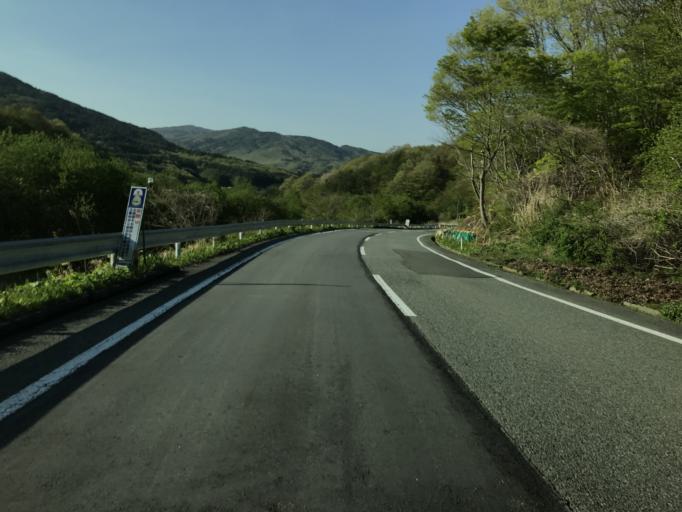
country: JP
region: Fukushima
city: Funehikimachi-funehiki
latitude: 37.5469
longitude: 140.7369
